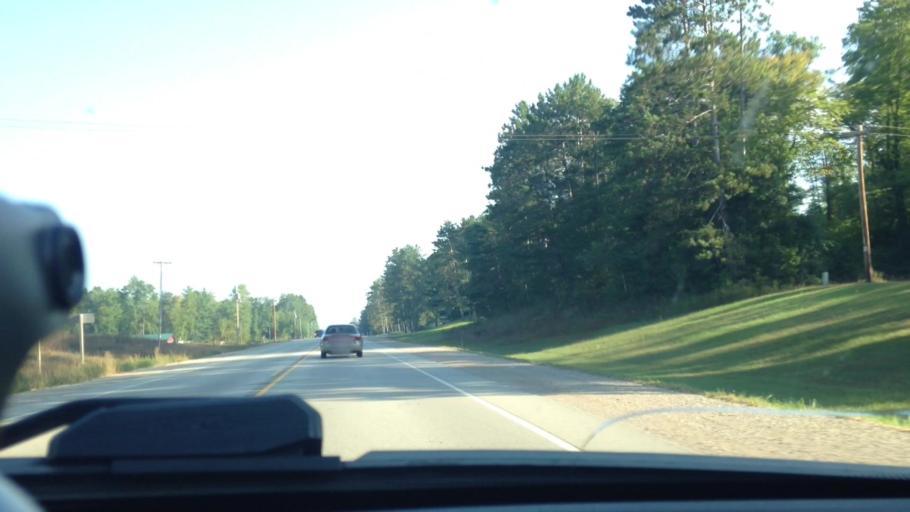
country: US
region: Wisconsin
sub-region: Marinette County
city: Peshtigo
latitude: 45.2464
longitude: -87.9937
